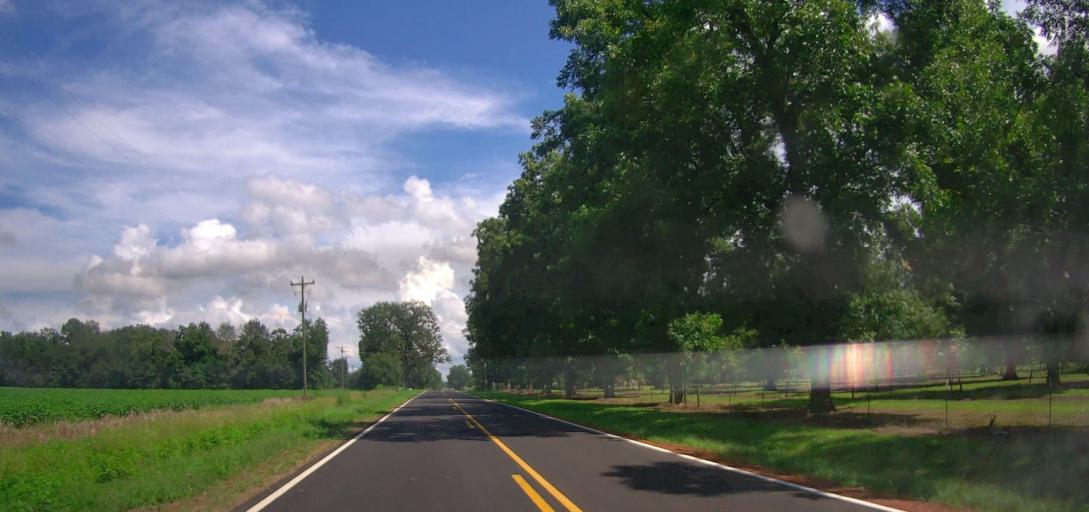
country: US
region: Georgia
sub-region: Macon County
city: Marshallville
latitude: 32.4727
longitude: -83.8817
